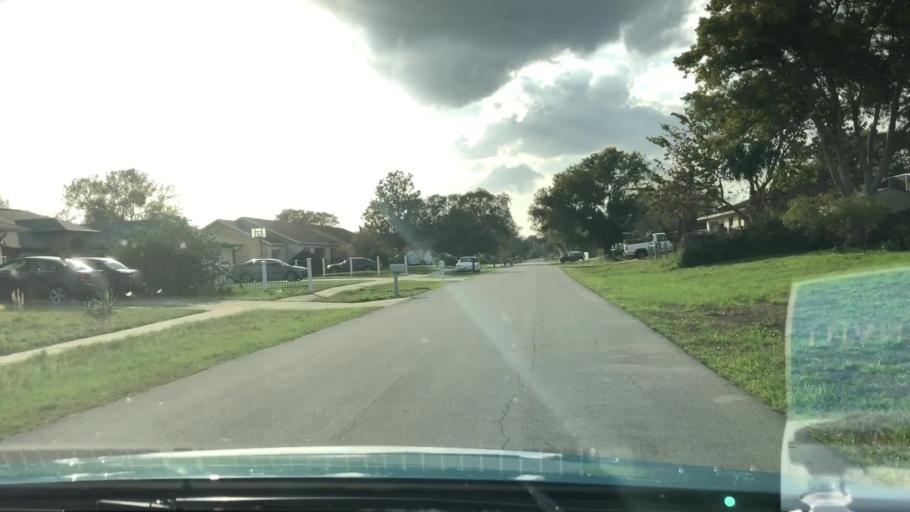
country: US
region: Florida
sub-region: Volusia County
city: Deltona
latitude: 28.8763
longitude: -81.2442
